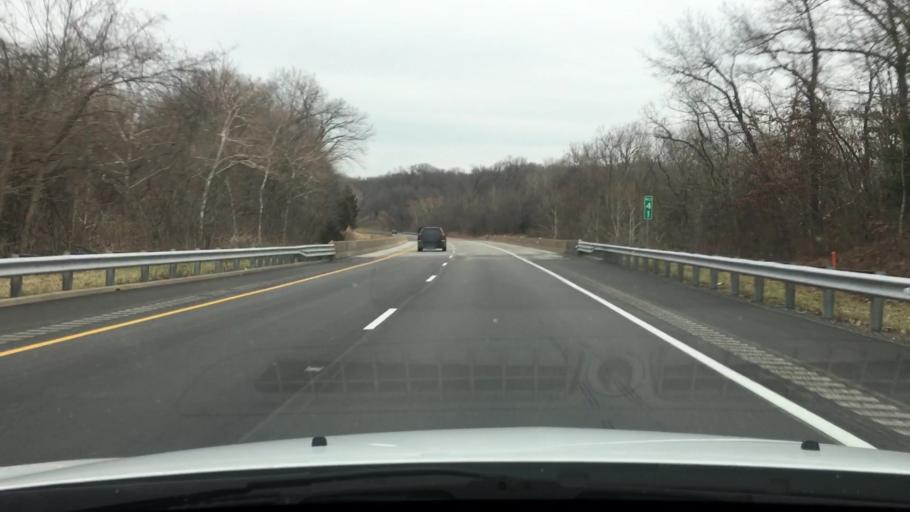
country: US
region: Illinois
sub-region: Pike County
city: Griggsville
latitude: 39.6812
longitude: -90.6581
